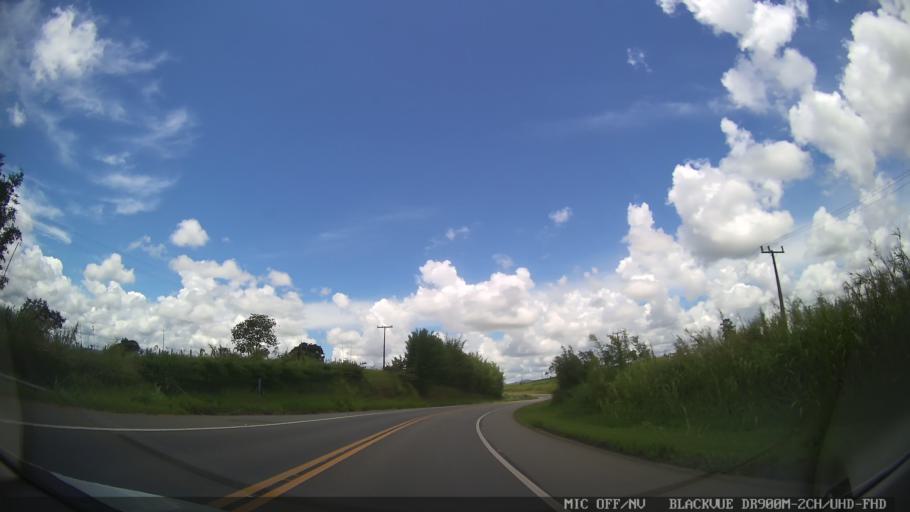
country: BR
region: Sao Paulo
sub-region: Braganca Paulista
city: Braganca Paulista
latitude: -22.8591
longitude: -46.6340
